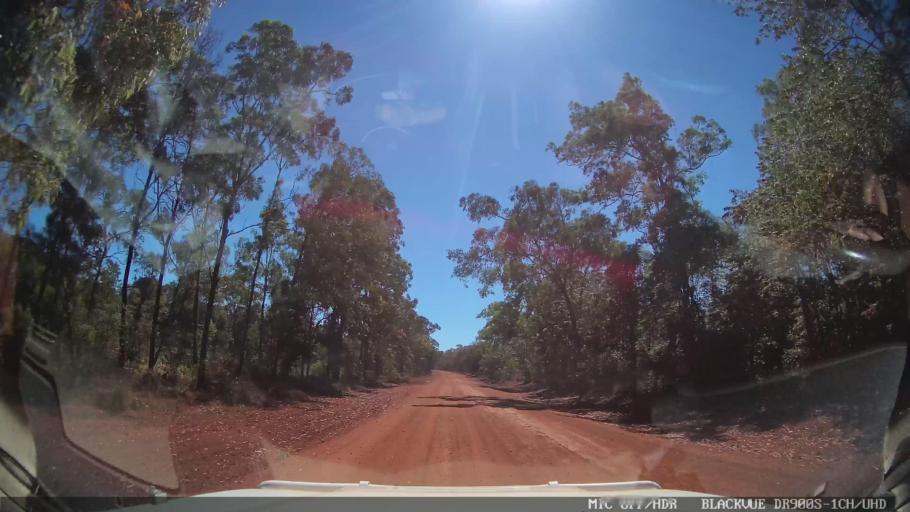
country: AU
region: Queensland
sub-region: Torres
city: Thursday Island
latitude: -10.8888
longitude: 142.4011
